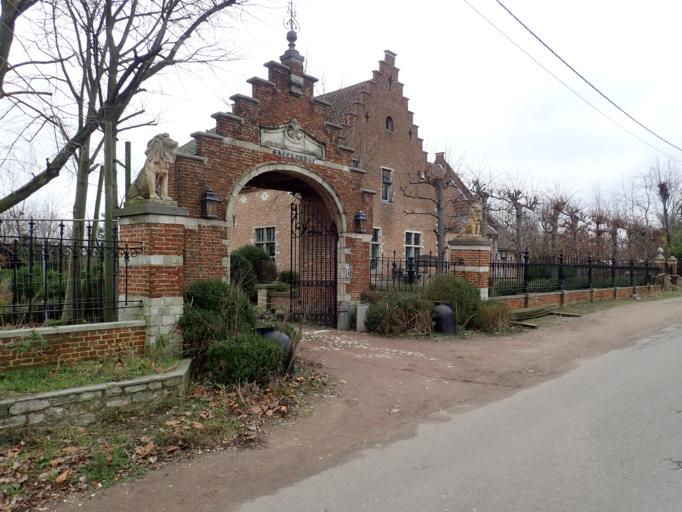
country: BE
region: Flanders
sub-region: Provincie Antwerpen
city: Boom
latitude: 51.0991
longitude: 4.3925
